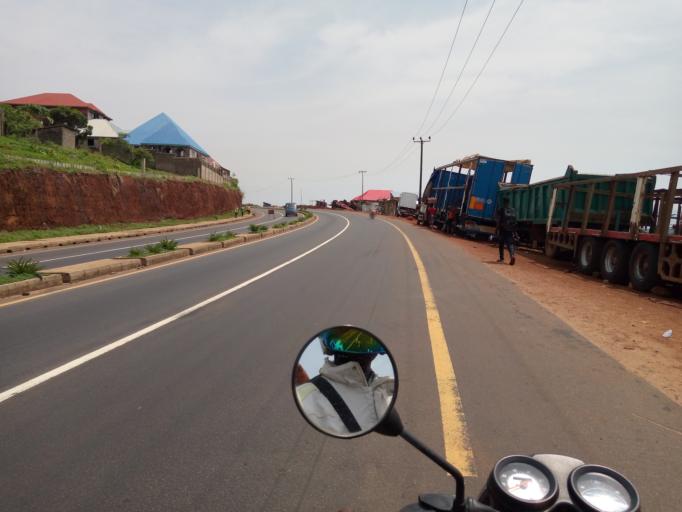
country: SL
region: Western Area
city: Waterloo
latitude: 8.3622
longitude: -13.0834
